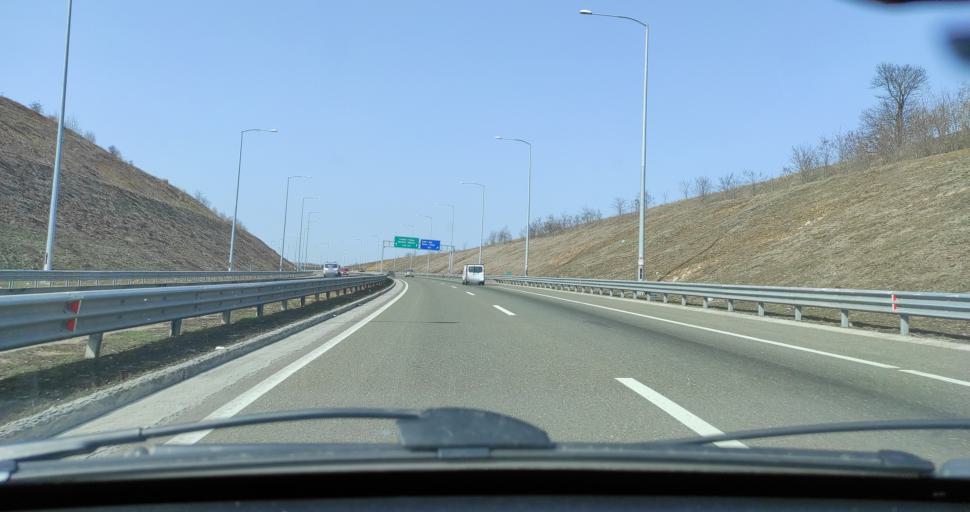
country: XK
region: Prizren
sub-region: Komuna e Therandes
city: Peqan
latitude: 42.4016
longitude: 20.8613
